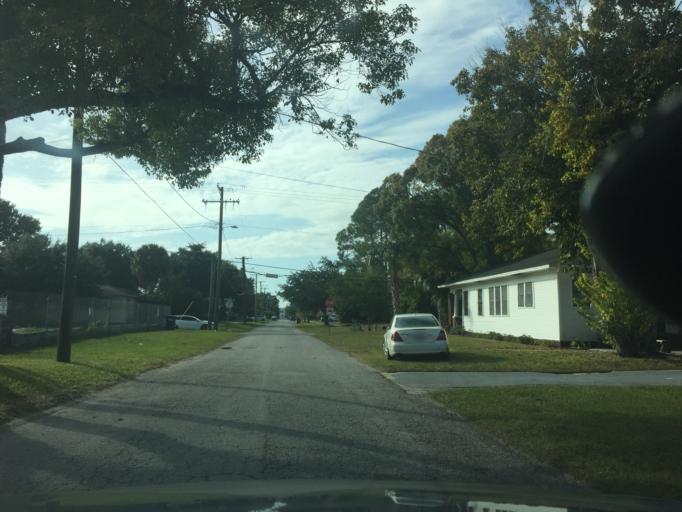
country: US
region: Florida
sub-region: Hillsborough County
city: Tampa
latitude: 27.9491
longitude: -82.4783
